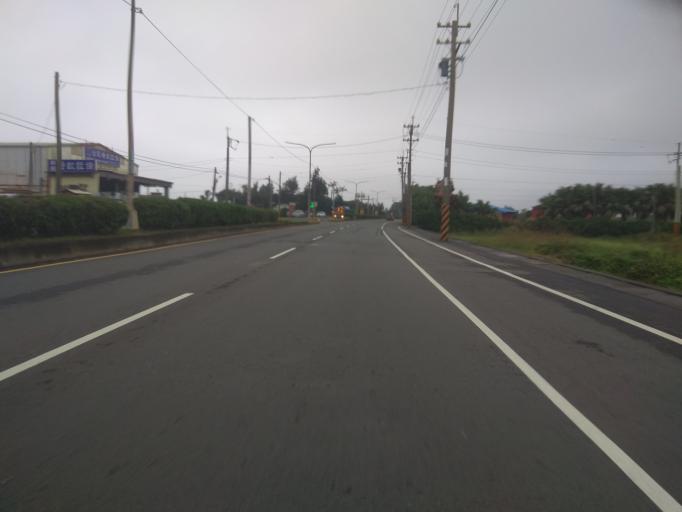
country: TW
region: Taiwan
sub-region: Hsinchu
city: Zhubei
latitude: 25.0217
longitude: 121.0581
